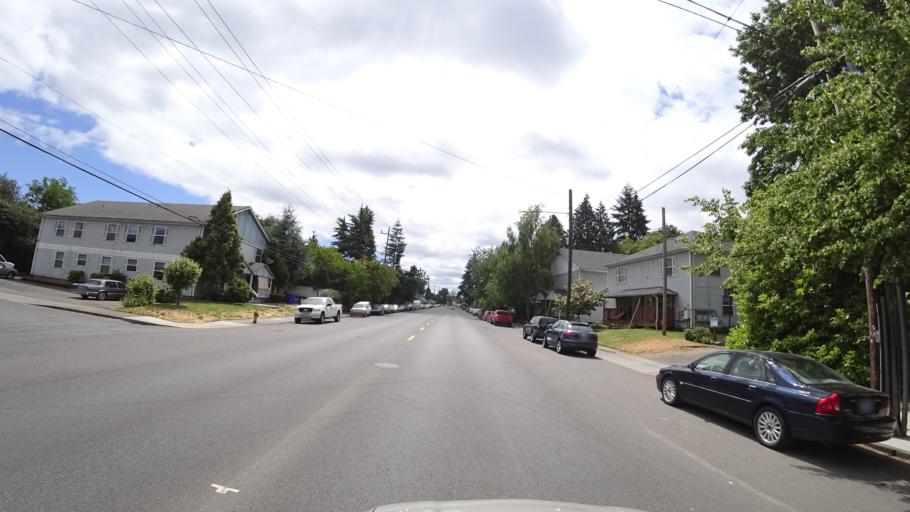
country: US
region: Oregon
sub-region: Washington County
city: West Haven
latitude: 45.5998
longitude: -122.7624
